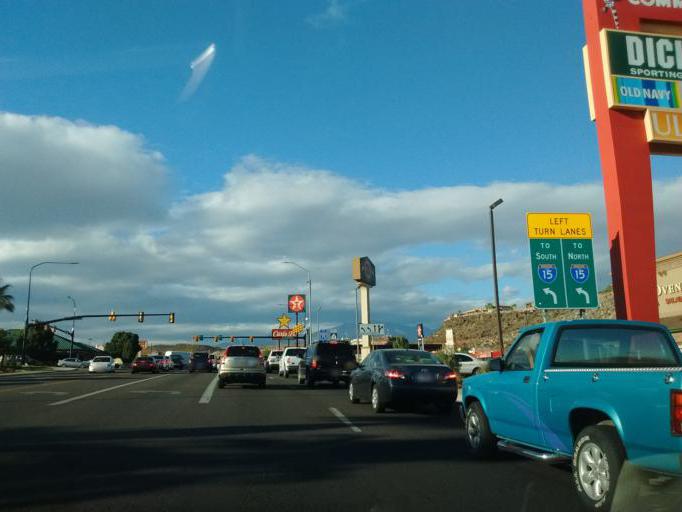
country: US
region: Utah
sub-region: Washington County
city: Saint George
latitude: 37.1089
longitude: -113.5545
